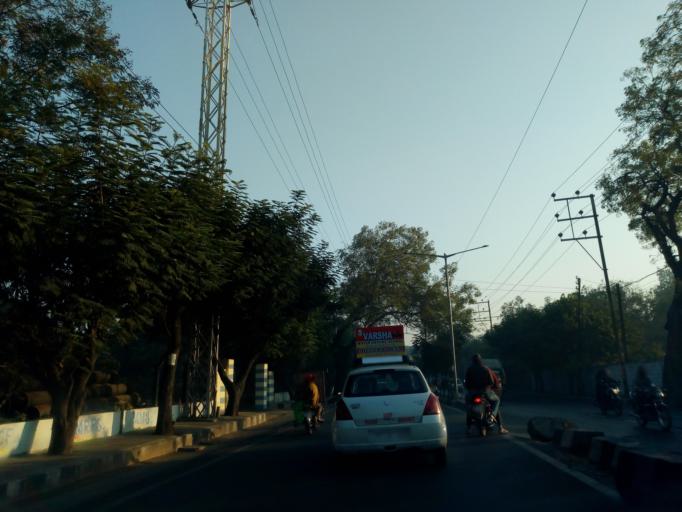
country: IN
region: Telangana
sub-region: Hyderabad
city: Malkajgiri
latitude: 17.4253
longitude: 78.5287
